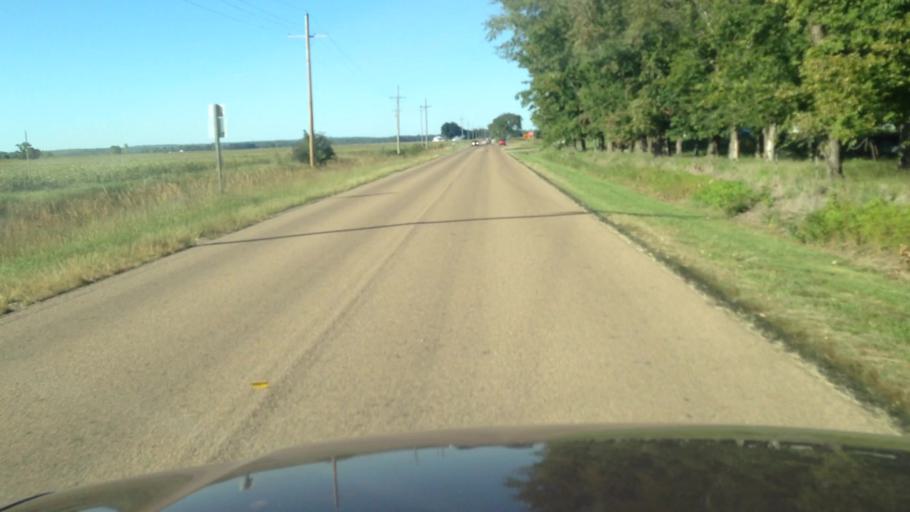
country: US
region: Kansas
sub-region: Douglas County
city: Eudora
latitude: 38.9398
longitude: -95.1489
